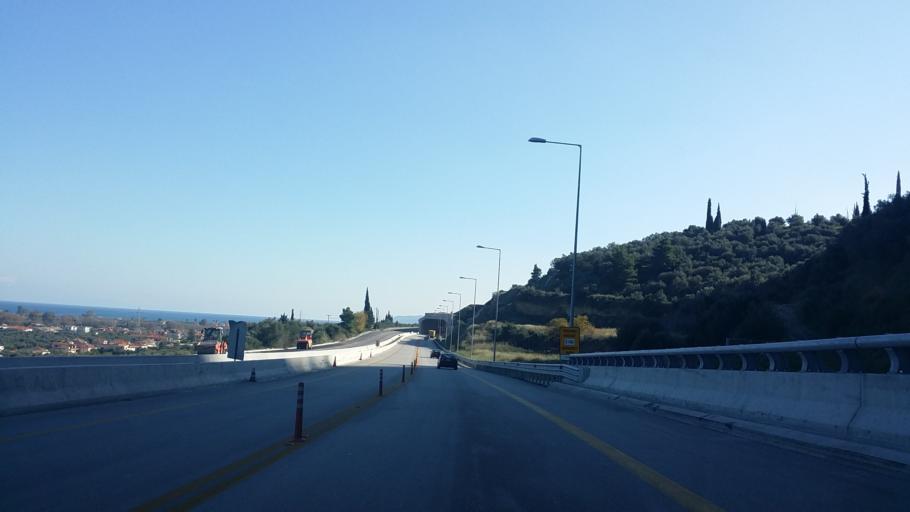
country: GR
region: West Greece
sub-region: Nomos Achaias
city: Temeni
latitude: 38.2095
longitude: 22.1300
